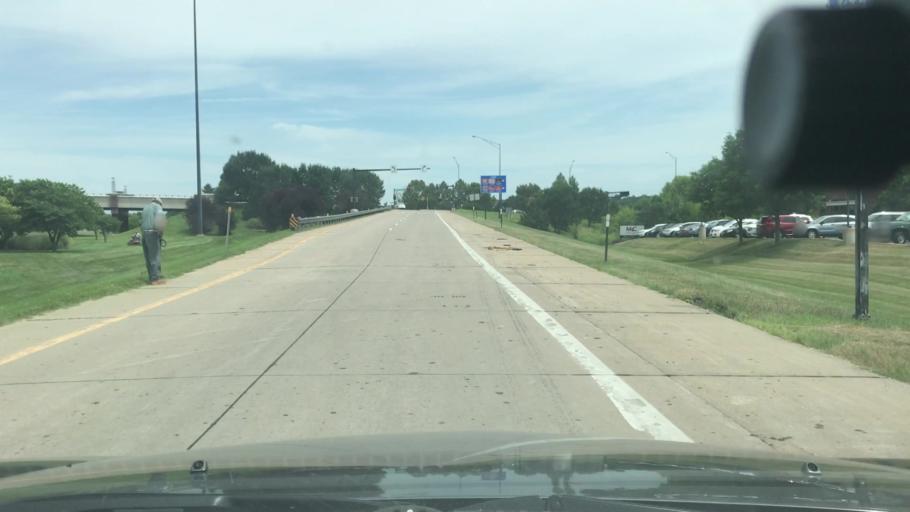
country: US
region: Missouri
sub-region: Saint Louis County
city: Chesterfield
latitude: 38.6703
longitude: -90.6020
